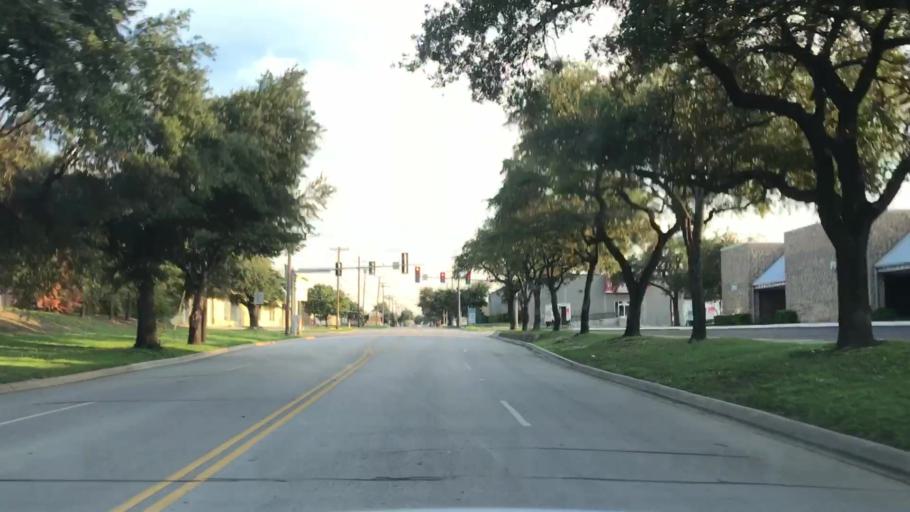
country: US
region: Texas
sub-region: Dallas County
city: Addison
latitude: 32.9339
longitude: -96.8306
